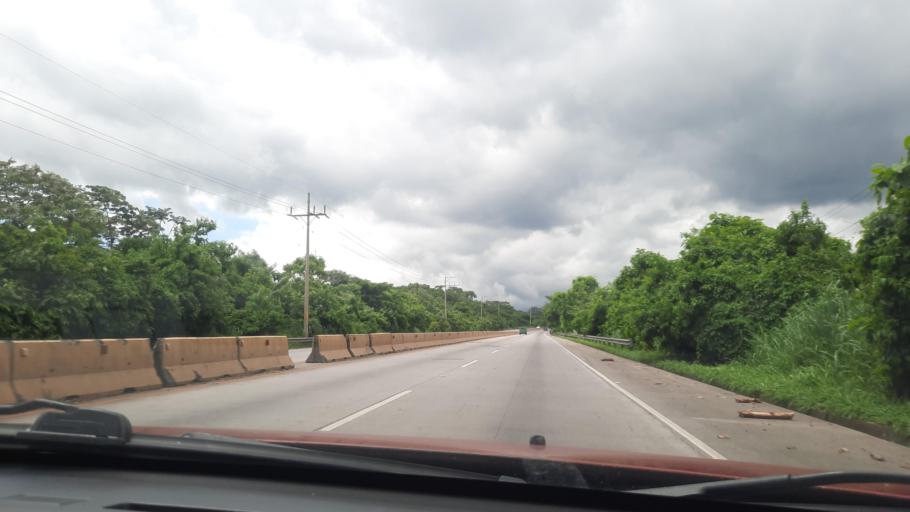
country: SV
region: Sonsonate
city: Sonzacate
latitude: 13.7317
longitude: -89.7009
